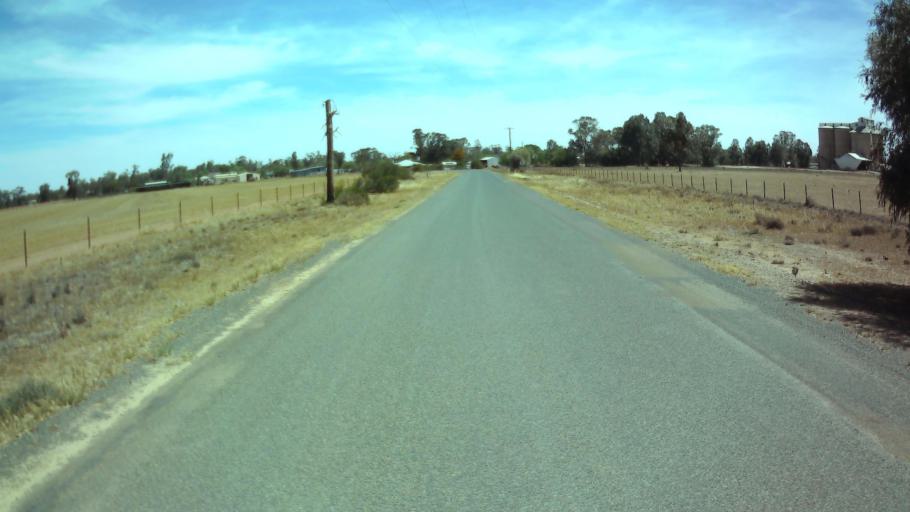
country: AU
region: New South Wales
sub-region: Weddin
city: Grenfell
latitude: -33.8373
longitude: 147.7462
